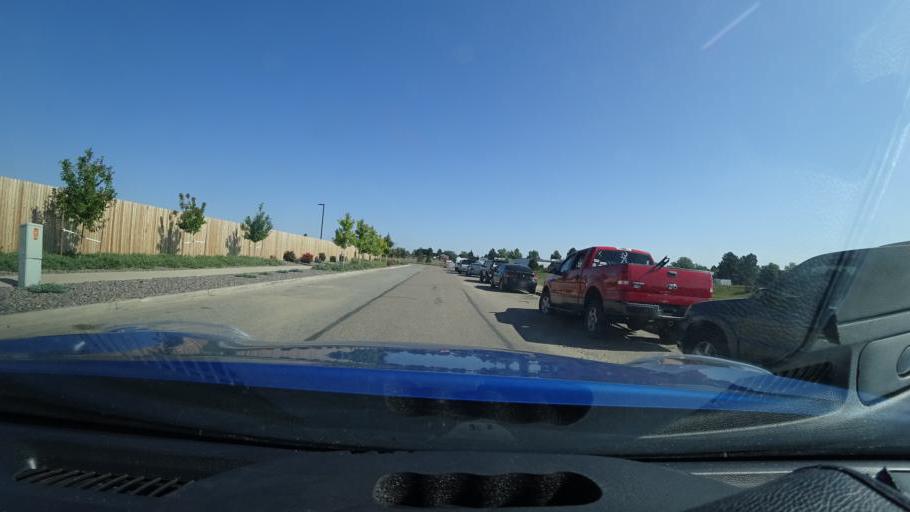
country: US
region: Colorado
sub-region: Adams County
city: Aurora
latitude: 39.7225
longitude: -104.7958
